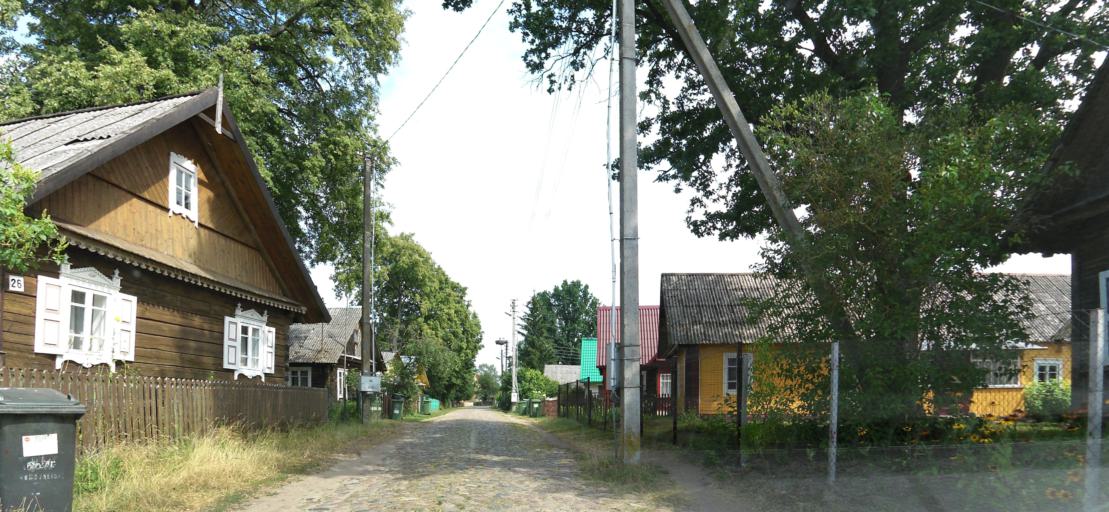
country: LT
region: Vilnius County
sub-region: Trakai
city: Rudiskes
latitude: 54.3662
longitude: 24.8460
